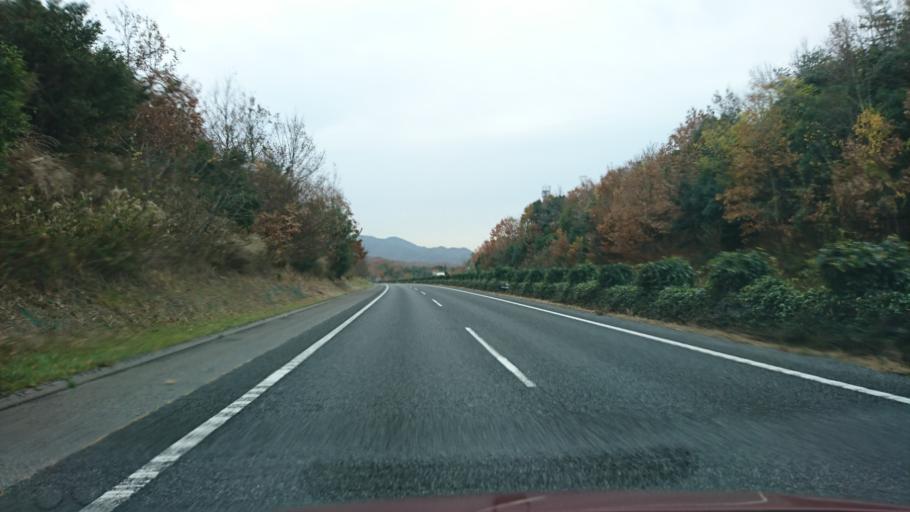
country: JP
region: Hyogo
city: Miki
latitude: 34.8036
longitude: 135.0345
